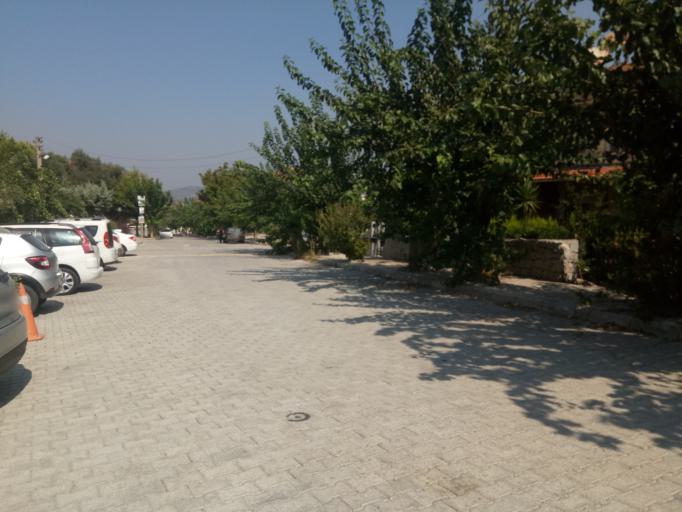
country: TR
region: Izmir
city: Urla
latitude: 38.3261
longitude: 26.7700
